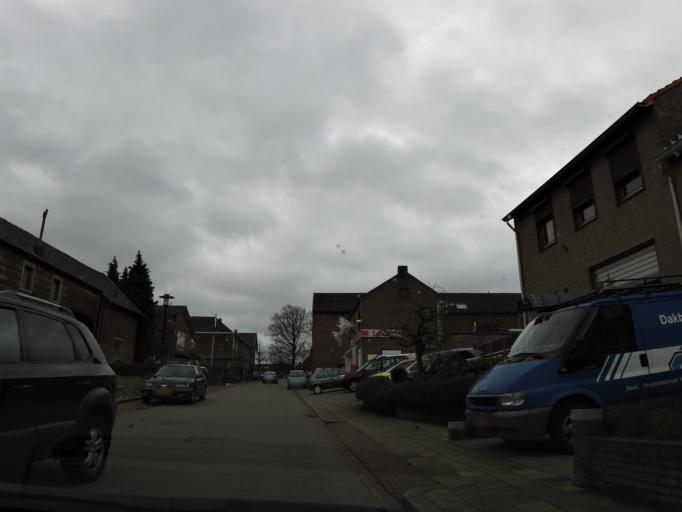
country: NL
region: Limburg
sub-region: Eijsden-Margraten
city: Margraten
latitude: 50.7912
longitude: 5.8081
